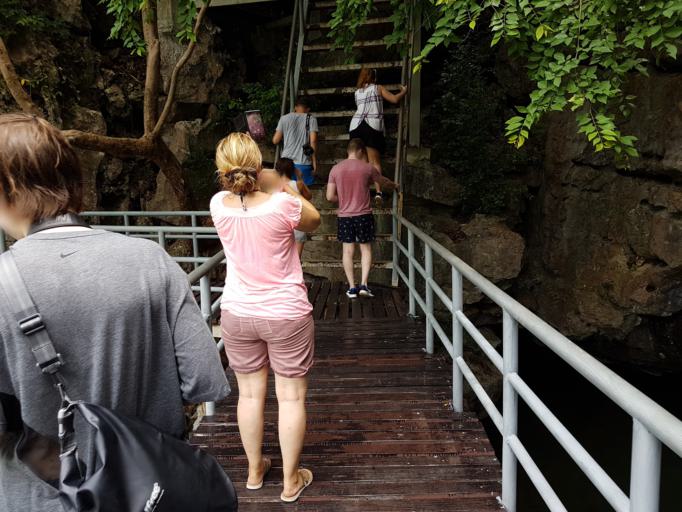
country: TH
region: Surat Thani
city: Ko Samui
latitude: 9.6572
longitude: 99.6664
